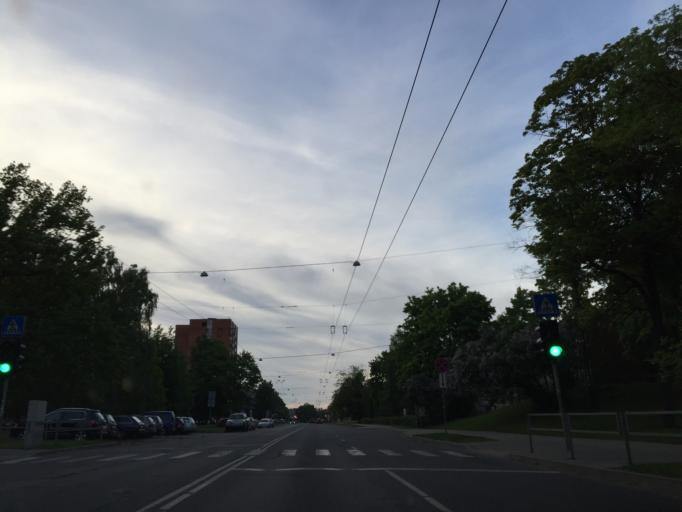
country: LV
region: Marupe
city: Marupe
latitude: 56.9535
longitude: 24.0534
